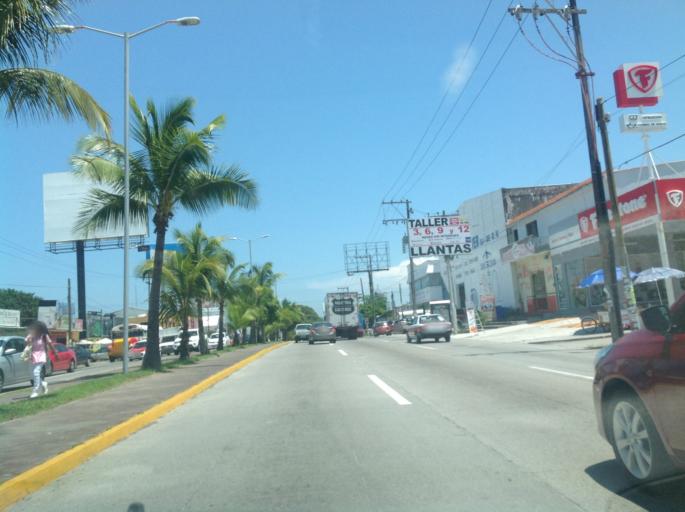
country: MX
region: Veracruz
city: Veracruz
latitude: 19.1426
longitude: -96.1225
